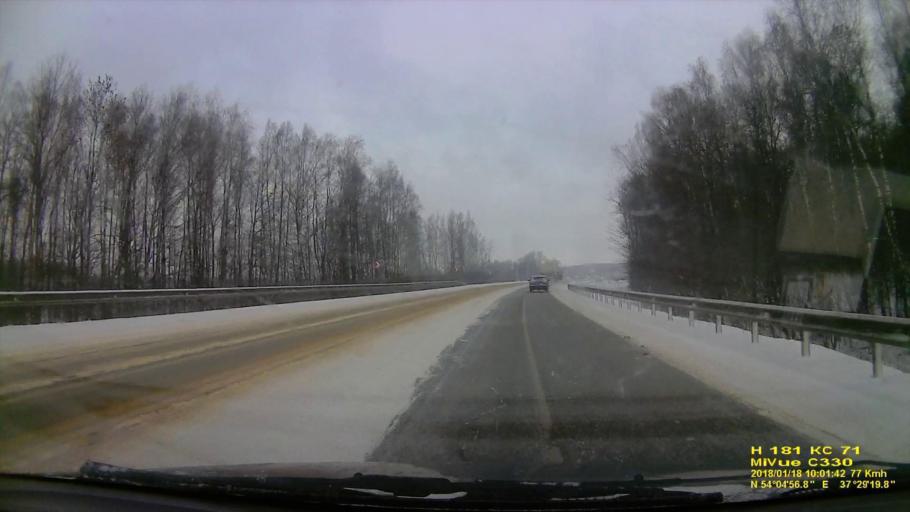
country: RU
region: Tula
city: Pervomayskiy
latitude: 54.0827
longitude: 37.4888
